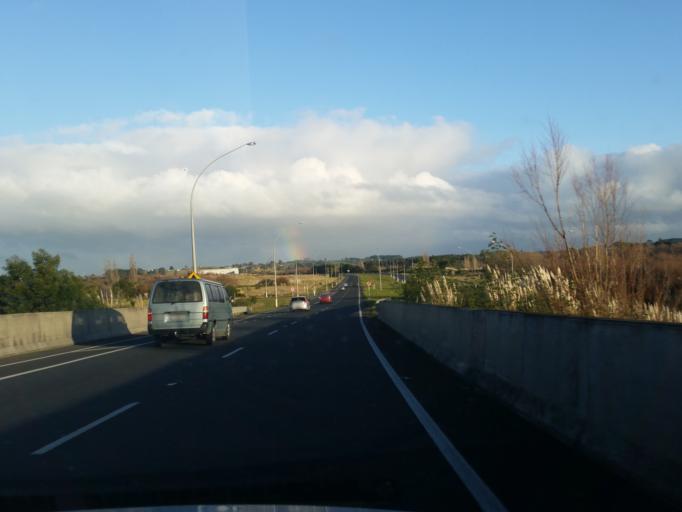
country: NZ
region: Waikato
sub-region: Waikato District
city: Te Kauwhata
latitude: -37.2937
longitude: 175.0596
